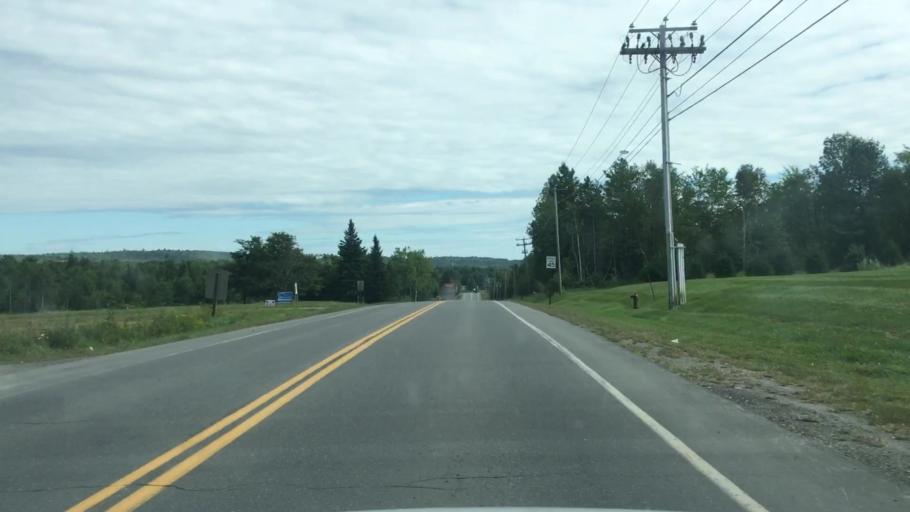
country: US
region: Maine
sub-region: Piscataquis County
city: Dover-Foxcroft
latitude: 45.1938
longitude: -69.2171
